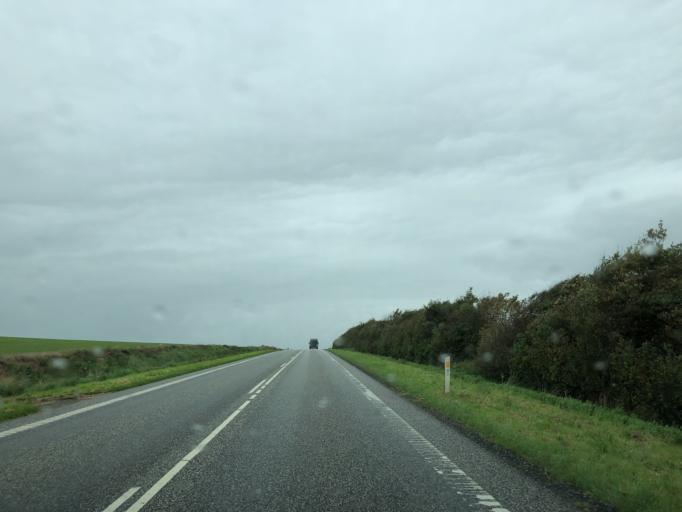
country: DK
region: Central Jutland
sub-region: Struer Kommune
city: Struer
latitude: 56.6110
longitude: 8.5276
